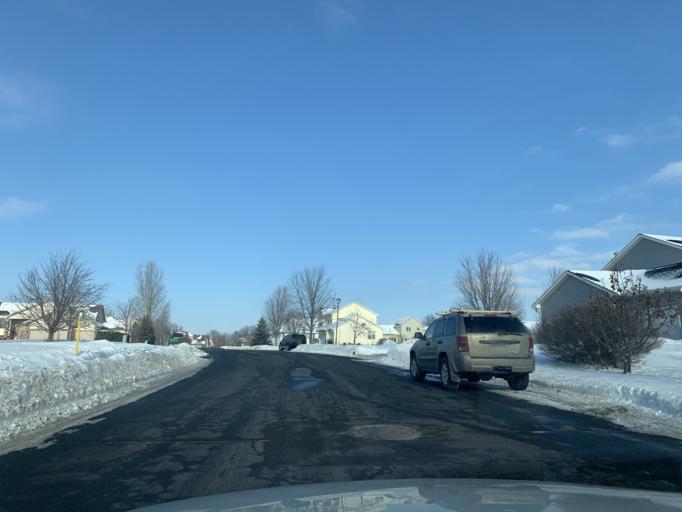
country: US
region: Minnesota
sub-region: Wright County
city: Buffalo
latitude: 45.2004
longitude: -93.8342
